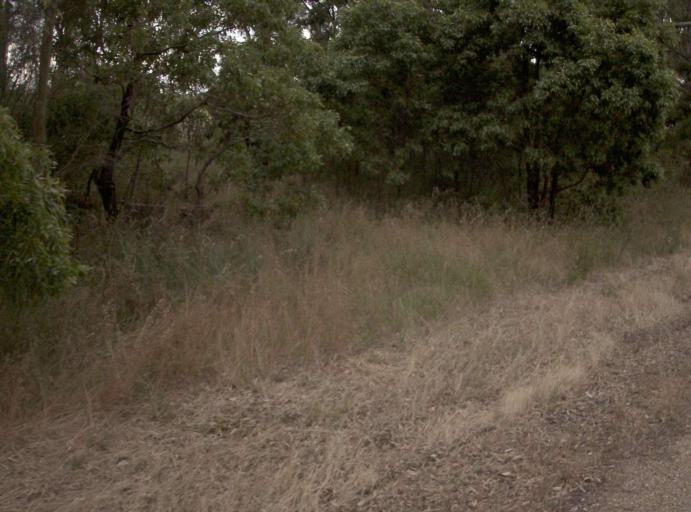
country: AU
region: Victoria
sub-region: Wellington
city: Sale
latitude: -38.0008
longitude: 147.3234
